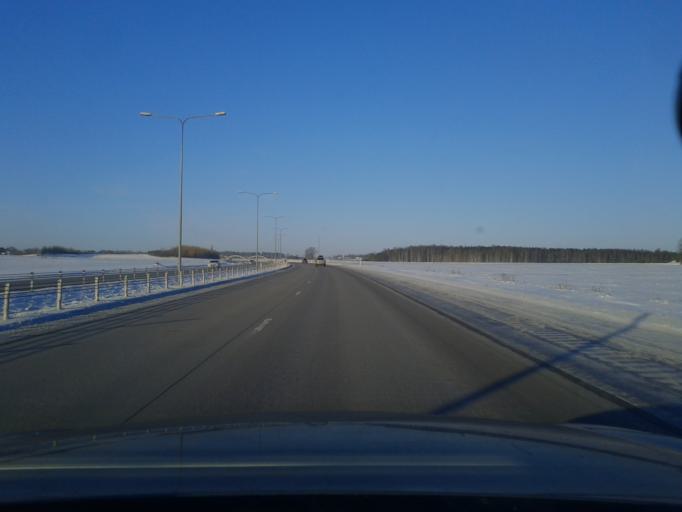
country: SE
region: Uppsala
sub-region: Uppsala Kommun
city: Saevja
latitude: 59.8609
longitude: 17.7248
